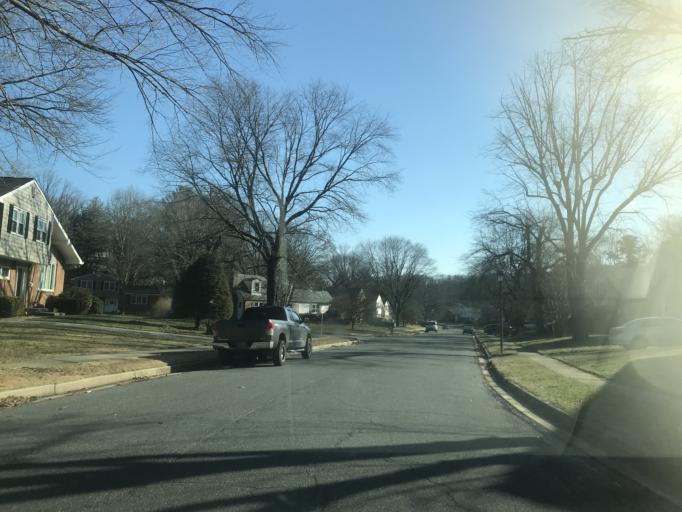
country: US
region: Maryland
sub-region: Baltimore County
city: Towson
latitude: 39.4021
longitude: -76.5823
